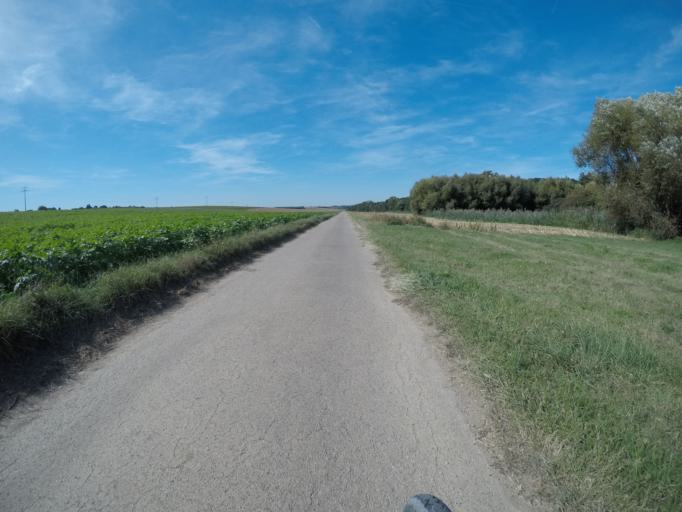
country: DE
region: Baden-Wuerttemberg
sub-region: Karlsruhe Region
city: Oberderdingen
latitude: 49.0765
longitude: 8.8199
